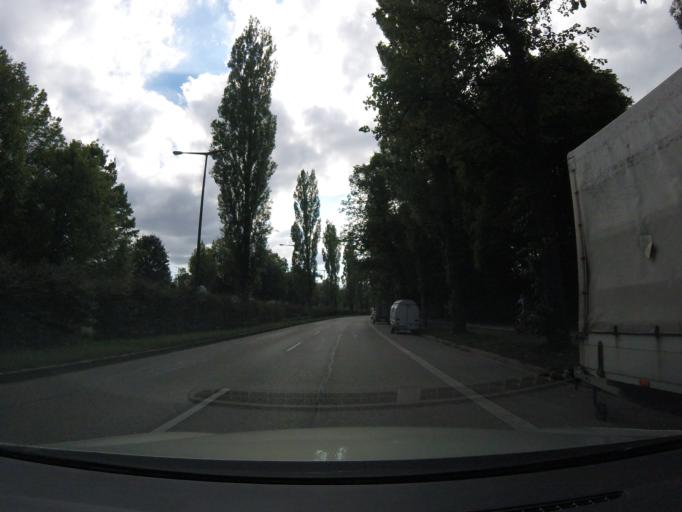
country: DE
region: Bavaria
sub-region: Upper Bavaria
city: Bogenhausen
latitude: 48.1538
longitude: 11.6336
